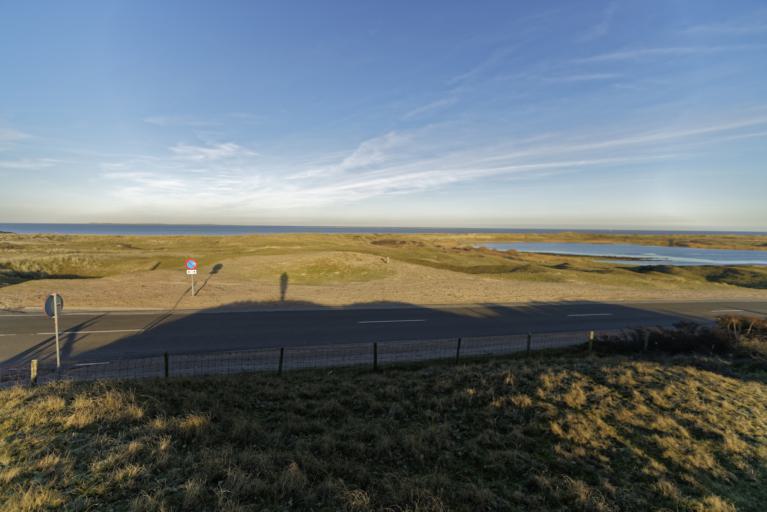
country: NL
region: North Holland
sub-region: Gemeente Texel
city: Den Burg
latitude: 53.1804
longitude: 4.8567
